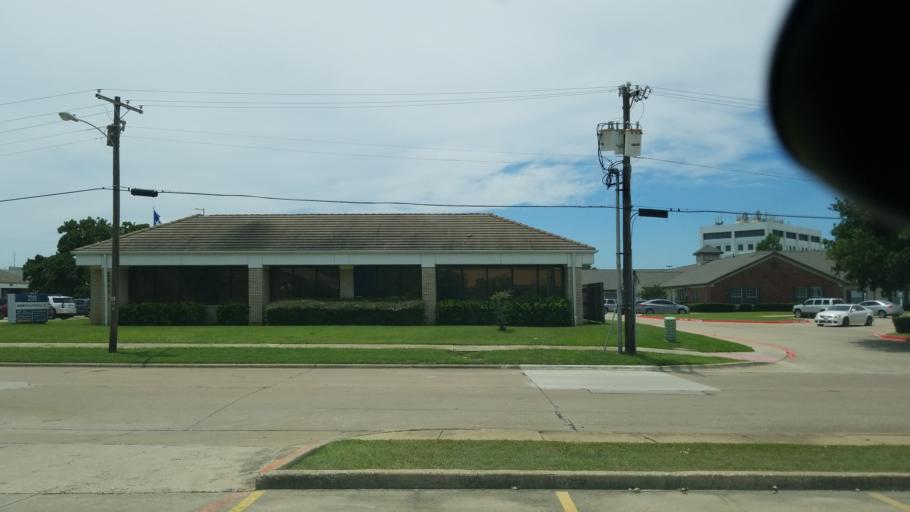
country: US
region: Texas
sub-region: Dallas County
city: Irving
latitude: 32.8395
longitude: -96.9719
